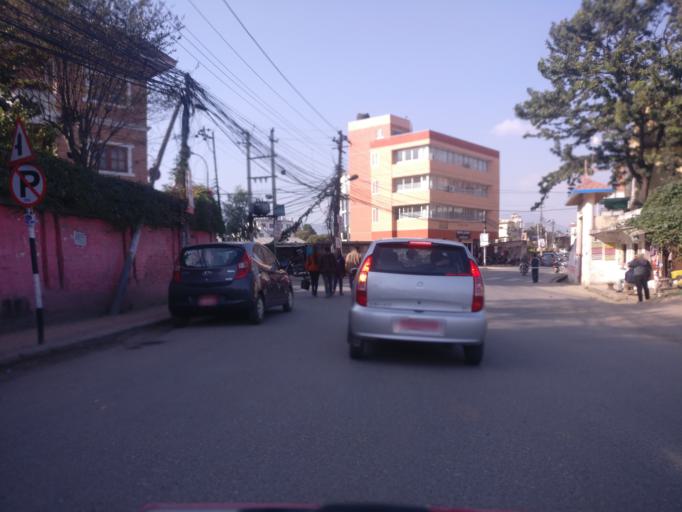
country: NP
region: Central Region
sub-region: Bagmati Zone
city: Patan
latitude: 27.6792
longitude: 85.3205
